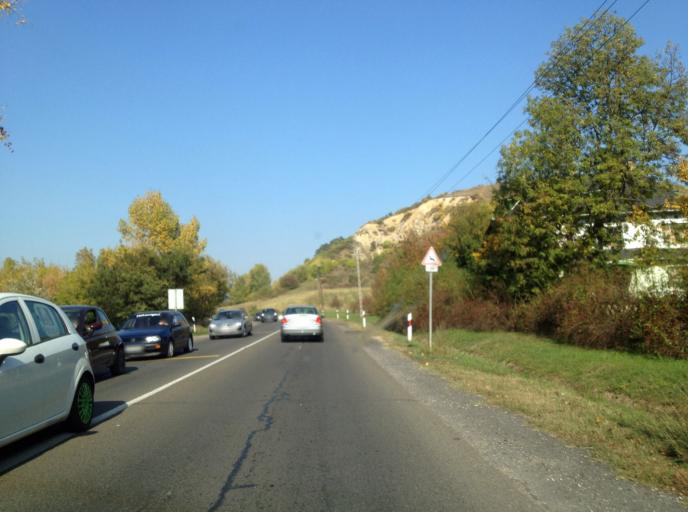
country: HU
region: Komarom-Esztergom
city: Dorog
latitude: 47.7478
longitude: 18.7366
